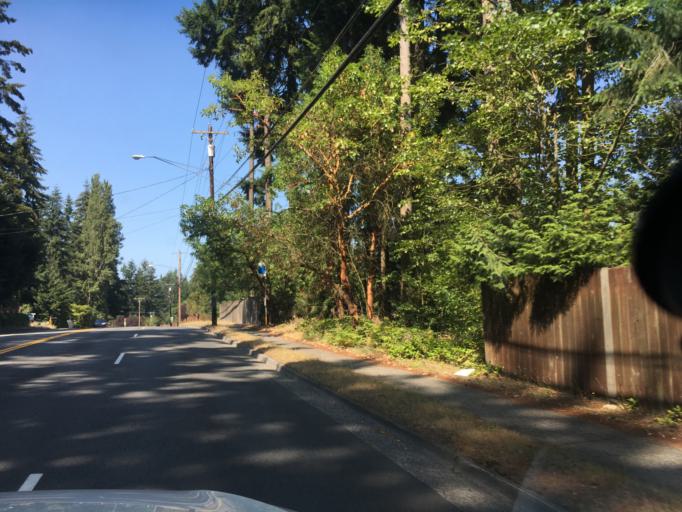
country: US
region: Washington
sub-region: Snohomish County
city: Esperance
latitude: 47.7843
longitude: -122.3664
